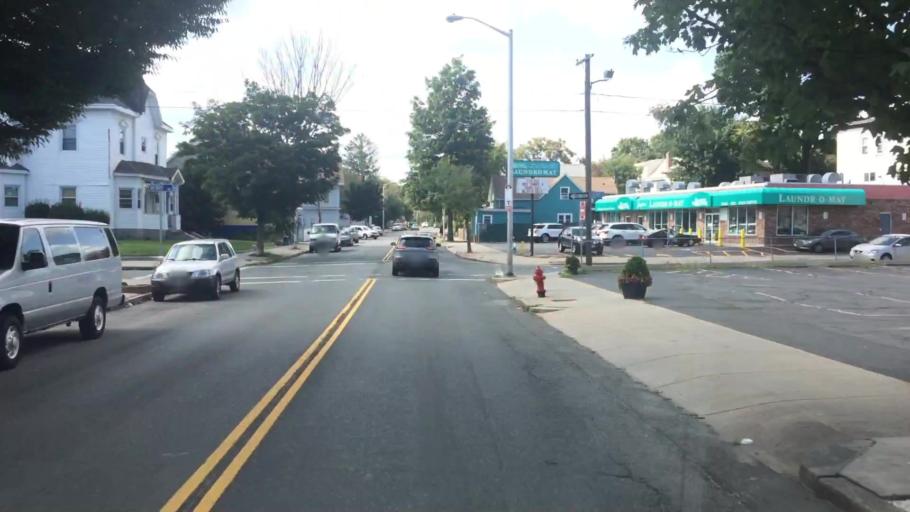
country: US
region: Massachusetts
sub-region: Essex County
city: Lynn
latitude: 42.4682
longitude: -70.9541
